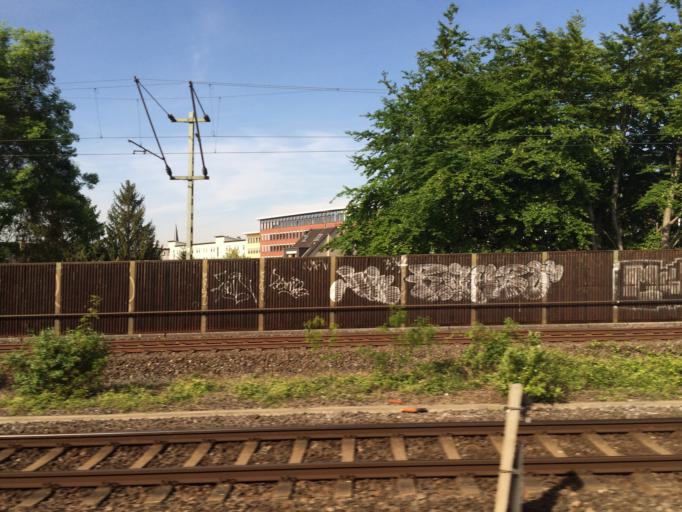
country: DE
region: North Rhine-Westphalia
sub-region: Regierungsbezirk Koln
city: Humboldtkolonie
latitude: 50.9344
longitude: 6.9998
